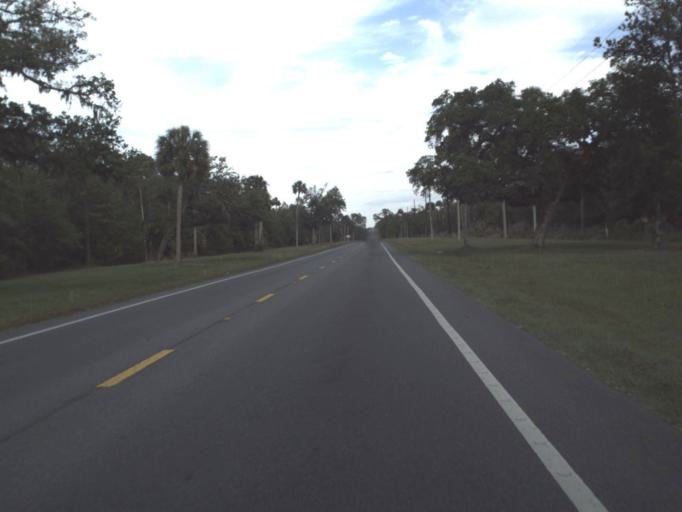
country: US
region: Florida
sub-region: Marion County
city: Silver Springs Shores
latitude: 29.2173
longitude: -82.0087
